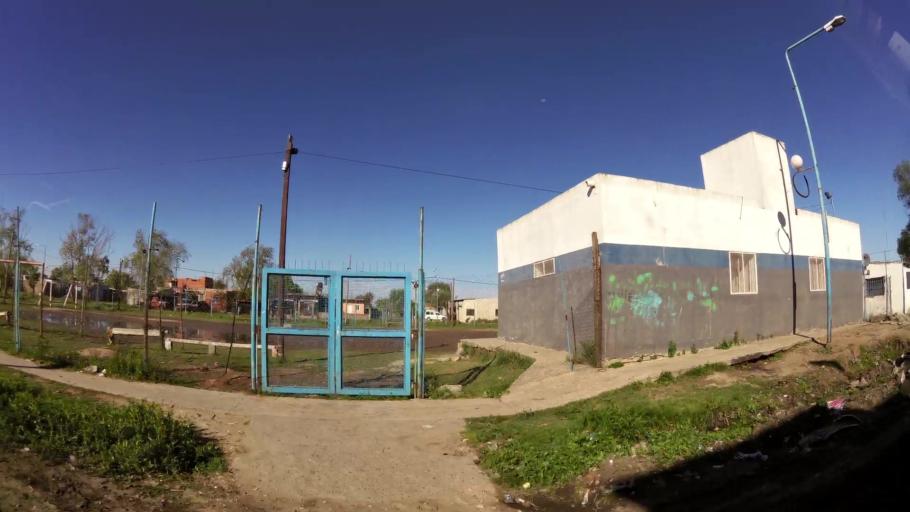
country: AR
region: Buenos Aires
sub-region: Partido de Quilmes
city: Quilmes
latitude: -34.7566
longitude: -58.3195
